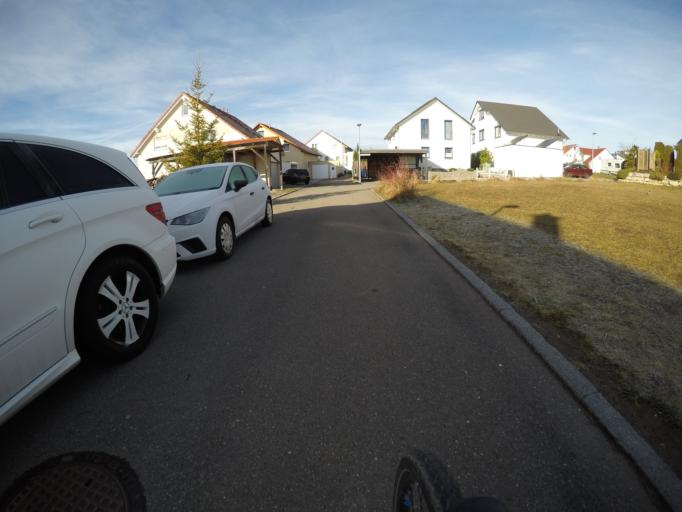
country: DE
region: Baden-Wuerttemberg
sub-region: Regierungsbezirk Stuttgart
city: Gartringen
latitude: 48.6468
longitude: 8.9031
